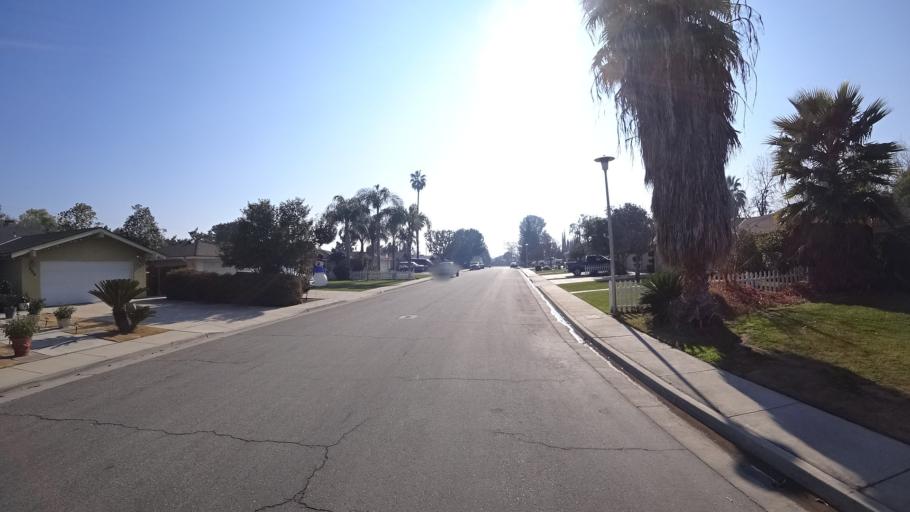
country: US
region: California
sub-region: Kern County
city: Greenacres
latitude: 35.3572
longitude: -119.0722
